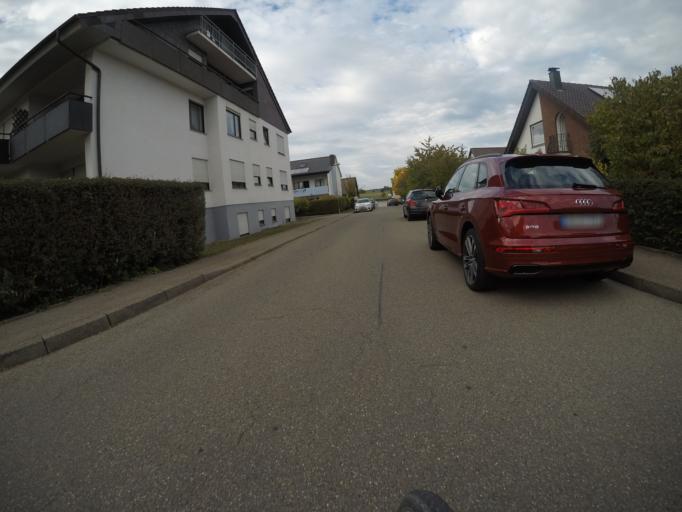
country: DE
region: Baden-Wuerttemberg
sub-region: Regierungsbezirk Stuttgart
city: Nufringen
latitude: 48.6250
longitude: 8.8914
